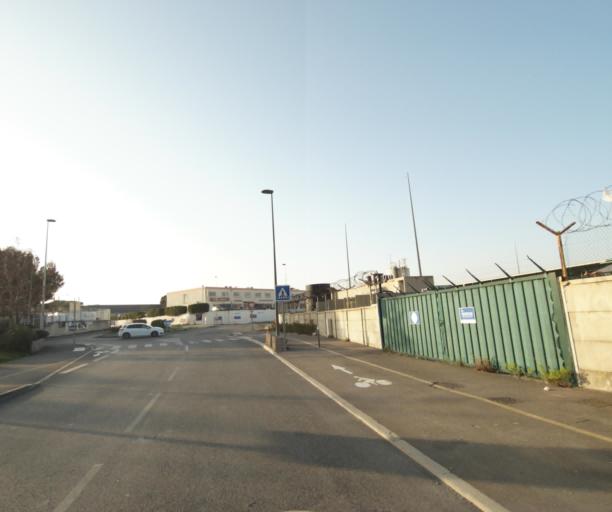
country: FR
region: Provence-Alpes-Cote d'Azur
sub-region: Departement des Bouches-du-Rhone
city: Saint-Victoret
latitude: 43.4341
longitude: 5.2432
